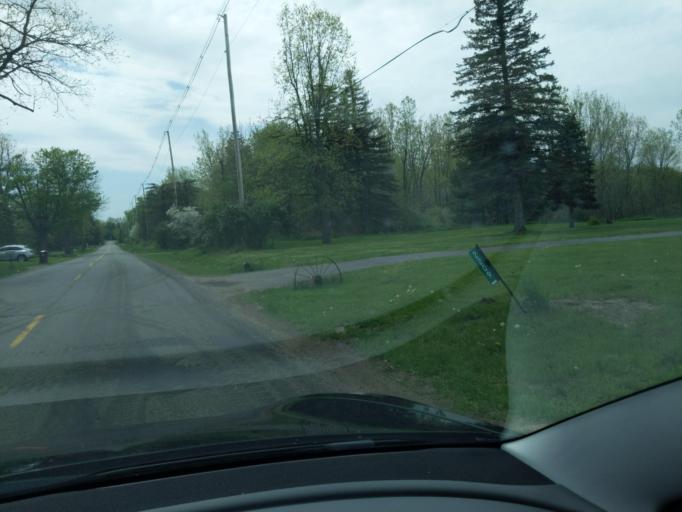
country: US
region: Michigan
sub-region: Ingham County
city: Holt
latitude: 42.6463
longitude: -84.5530
